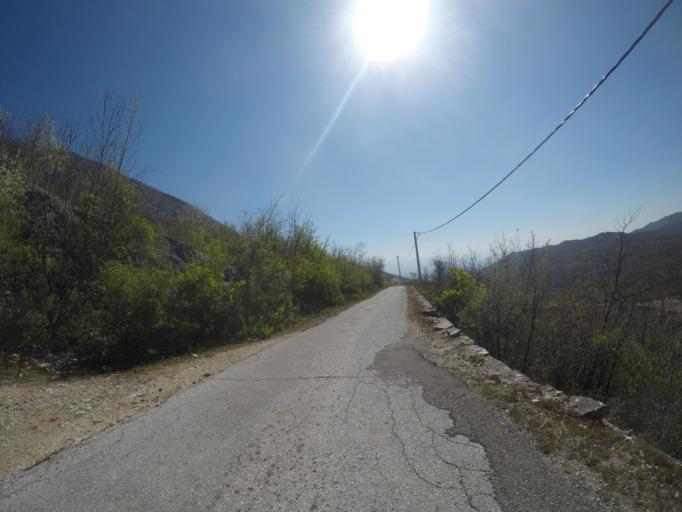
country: ME
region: Danilovgrad
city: Danilovgrad
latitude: 42.5292
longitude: 19.0311
